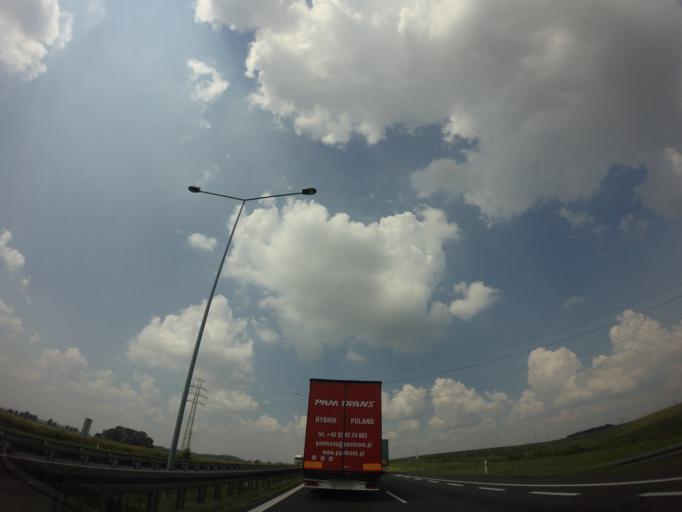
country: PL
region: Silesian Voivodeship
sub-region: Powiat gliwicki
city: Rudziniec
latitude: 50.3955
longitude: 18.4404
